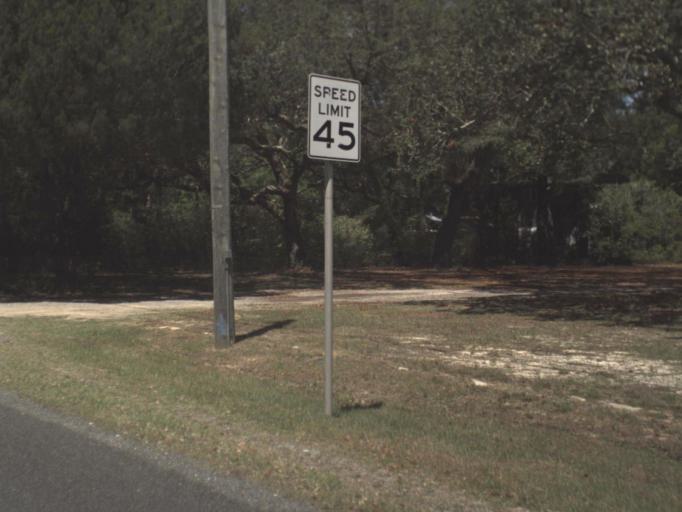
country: US
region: Florida
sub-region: Escambia County
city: Myrtle Grove
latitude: 30.3978
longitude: -87.4032
